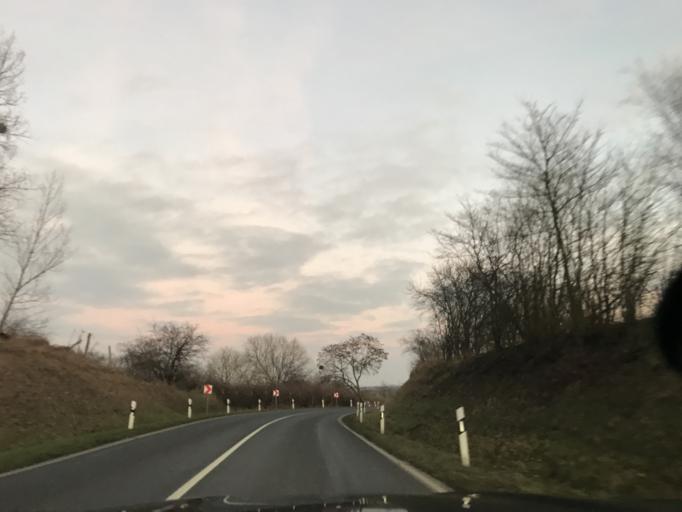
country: DE
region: Brandenburg
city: Ketzin
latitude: 52.5264
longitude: 12.8348
